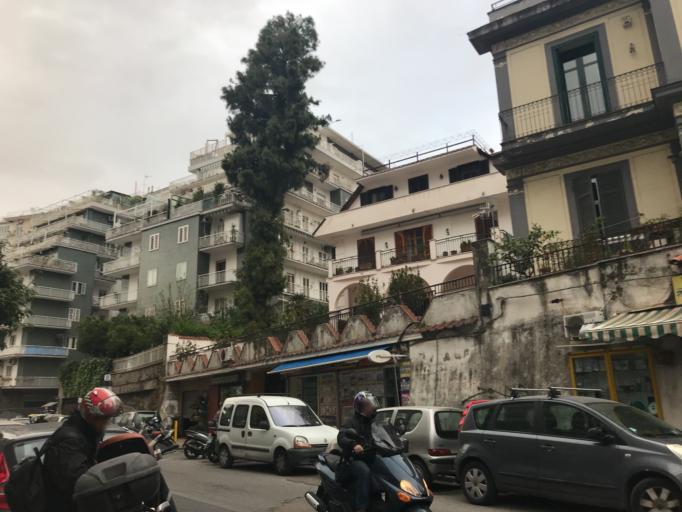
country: IT
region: Campania
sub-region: Provincia di Napoli
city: Napoli
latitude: 40.8528
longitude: 14.2249
